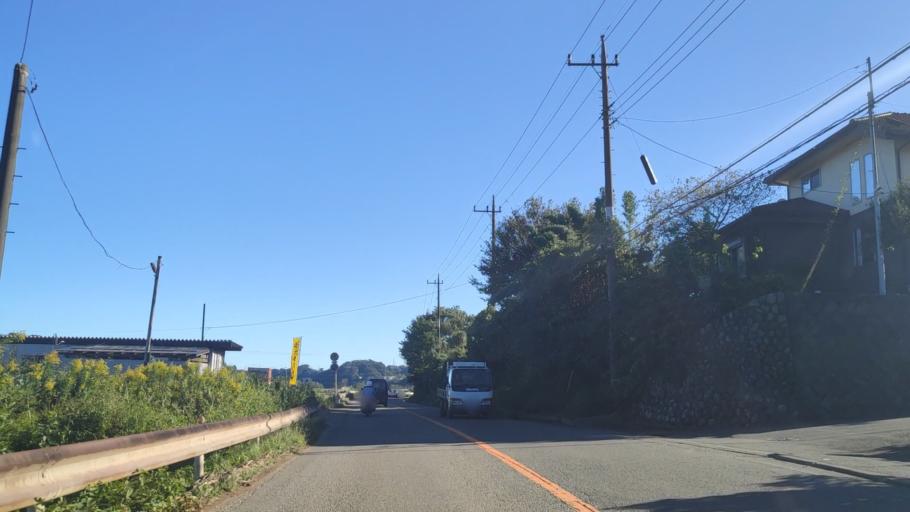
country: JP
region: Tokyo
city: Hachioji
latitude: 35.5581
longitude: 139.3190
